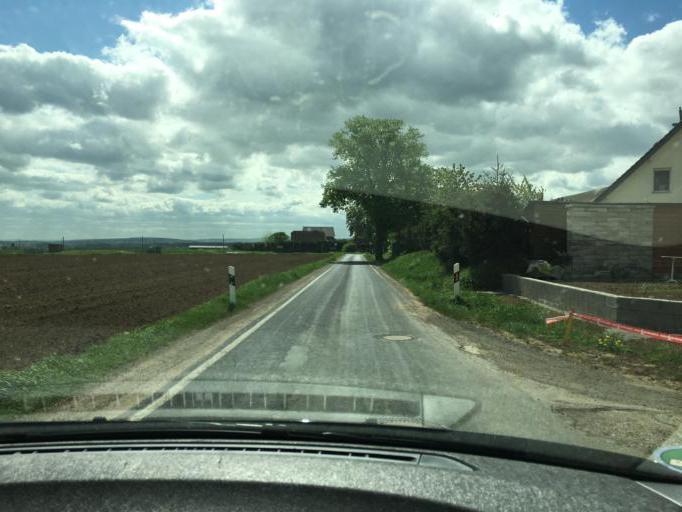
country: DE
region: North Rhine-Westphalia
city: Zulpich
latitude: 50.6778
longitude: 6.6191
